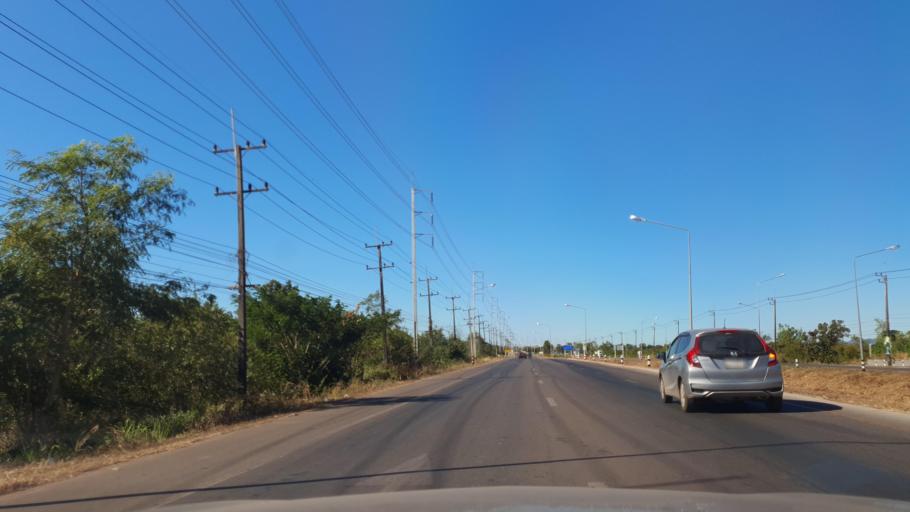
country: TH
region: Nakhon Phanom
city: Nakhon Phanom
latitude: 17.4014
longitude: 104.7643
